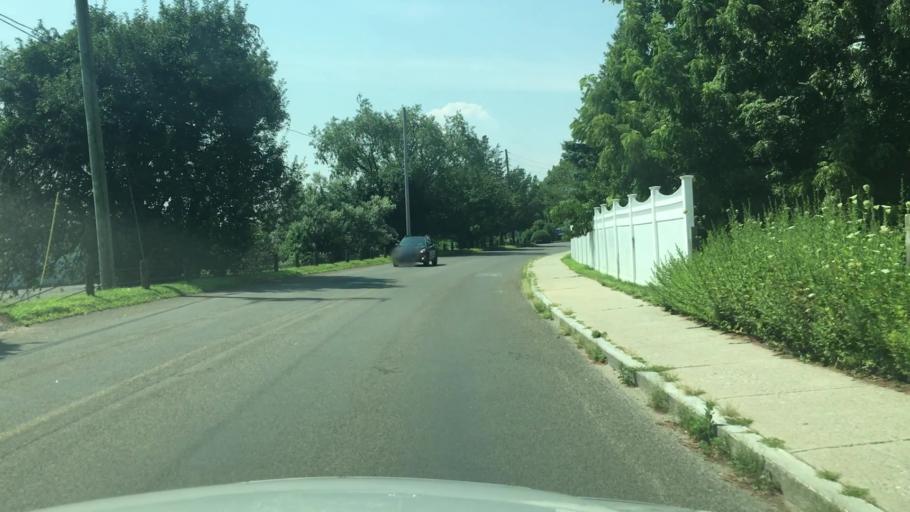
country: US
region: Connecticut
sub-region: New Haven County
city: Guilford Center
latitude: 41.2734
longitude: -72.6719
